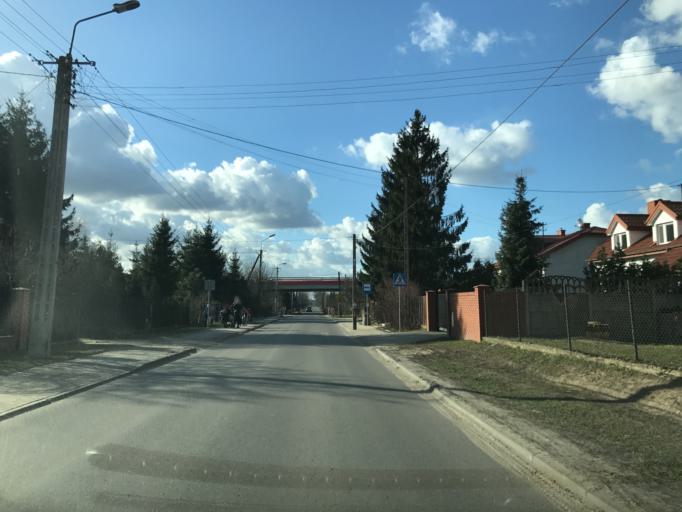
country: PL
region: Masovian Voivodeship
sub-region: Powiat wolominski
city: Radzymin
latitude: 52.3903
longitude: 21.1990
